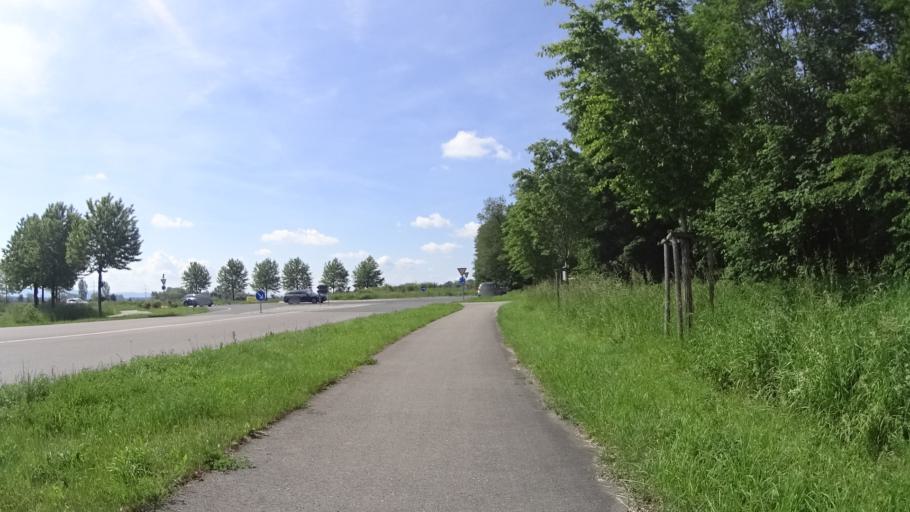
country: DE
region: Baden-Wuerttemberg
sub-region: Freiburg Region
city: Willstatt
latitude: 48.4953
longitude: 7.8215
